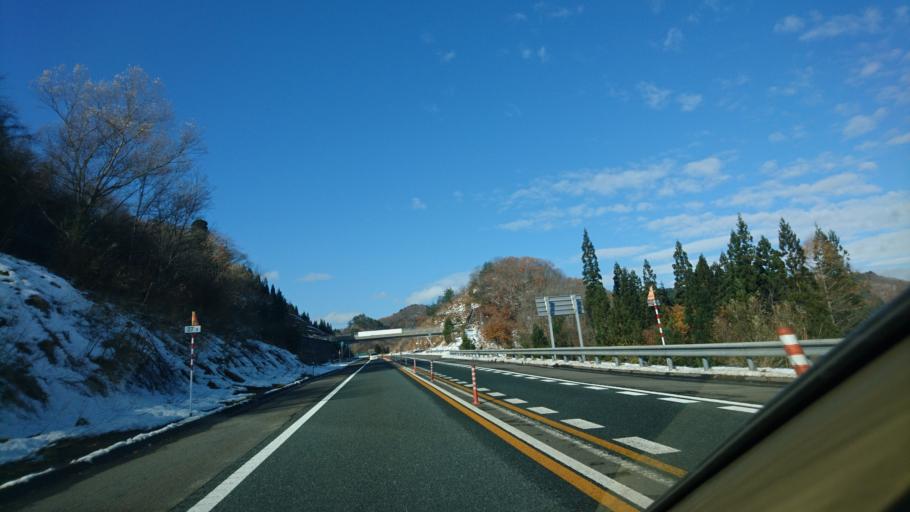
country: JP
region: Akita
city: Yokotemachi
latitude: 39.3090
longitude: 140.7769
